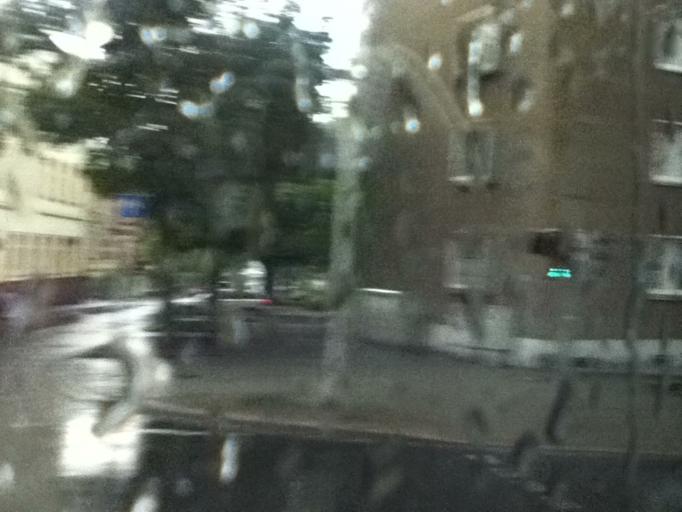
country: DE
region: Thuringia
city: Gera
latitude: 50.8801
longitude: 12.0787
